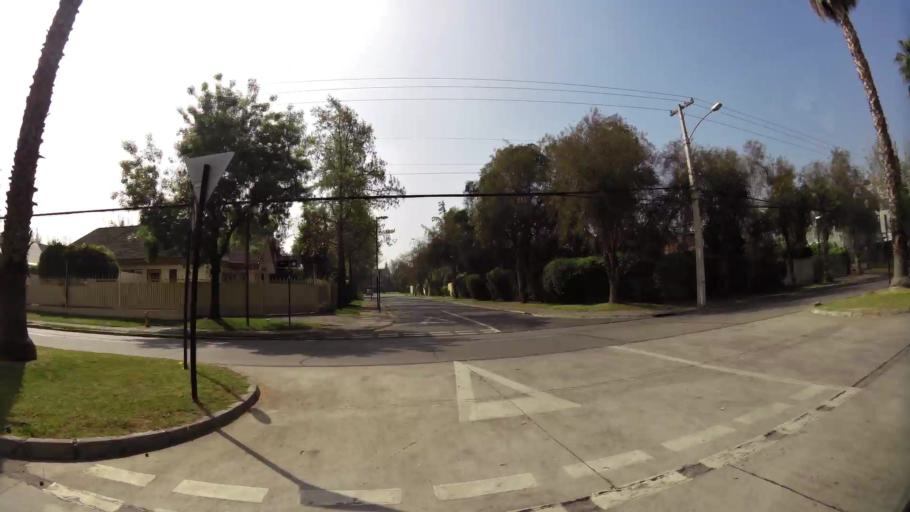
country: CL
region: Santiago Metropolitan
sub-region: Provincia de Santiago
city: Villa Presidente Frei, Nunoa, Santiago, Chile
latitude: -33.3787
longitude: -70.5833
